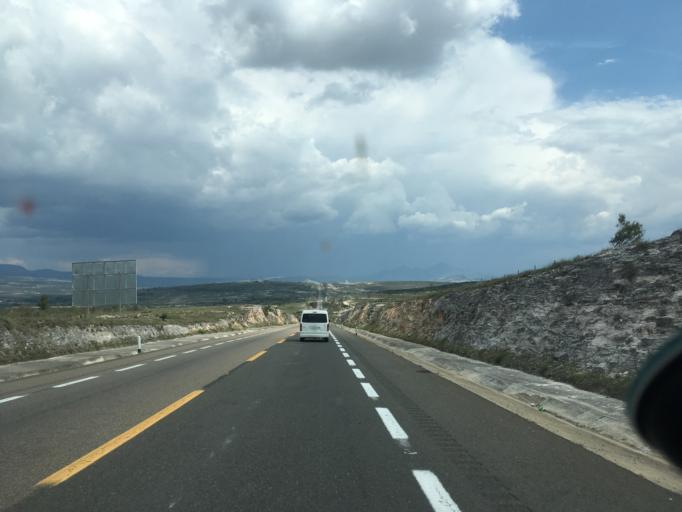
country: MX
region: Oaxaca
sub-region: Villa Tejupam de la Union
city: Villa Tejupam de la Union
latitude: 17.8058
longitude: -97.3654
